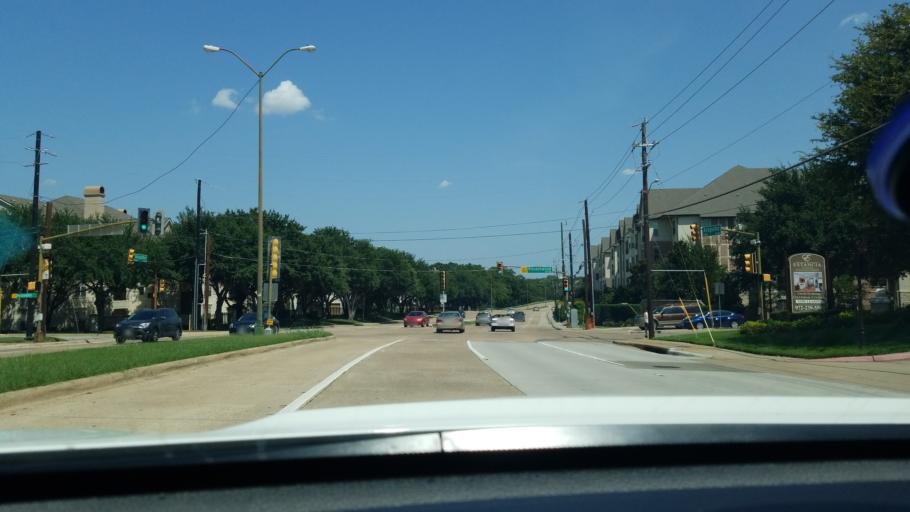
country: US
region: Texas
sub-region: Dallas County
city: Addison
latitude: 32.9612
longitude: -96.8156
